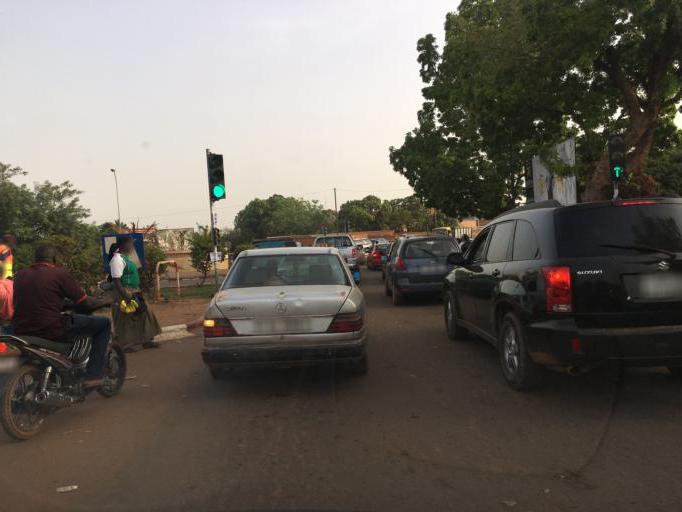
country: BF
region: Centre
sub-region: Kadiogo Province
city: Ouagadougou
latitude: 12.3681
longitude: -1.5068
